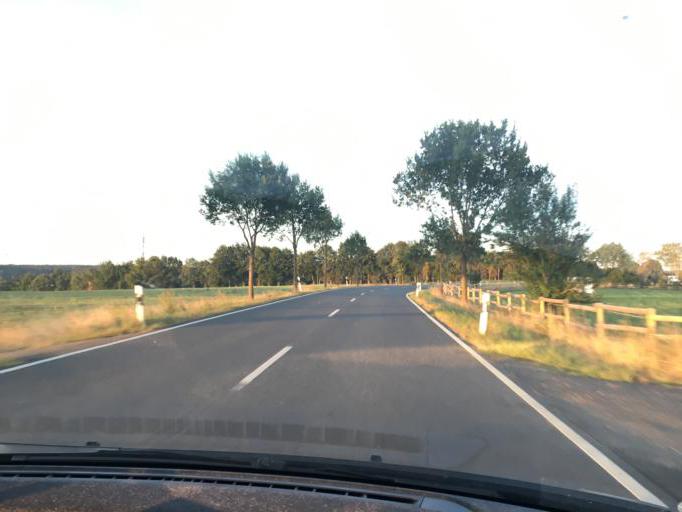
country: DE
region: North Rhine-Westphalia
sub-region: Regierungsbezirk Koln
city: Hurtgenwald
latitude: 50.6708
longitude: 6.3445
